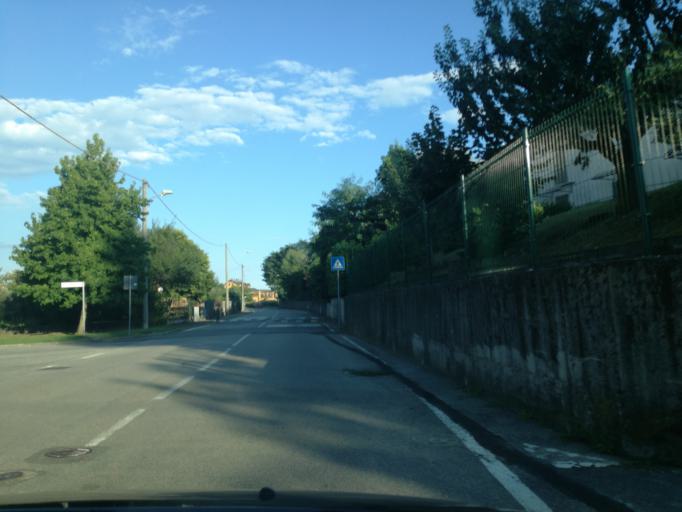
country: IT
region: Lombardy
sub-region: Provincia di Lecco
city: Paderno d'Adda
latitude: 45.6780
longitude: 9.4480
